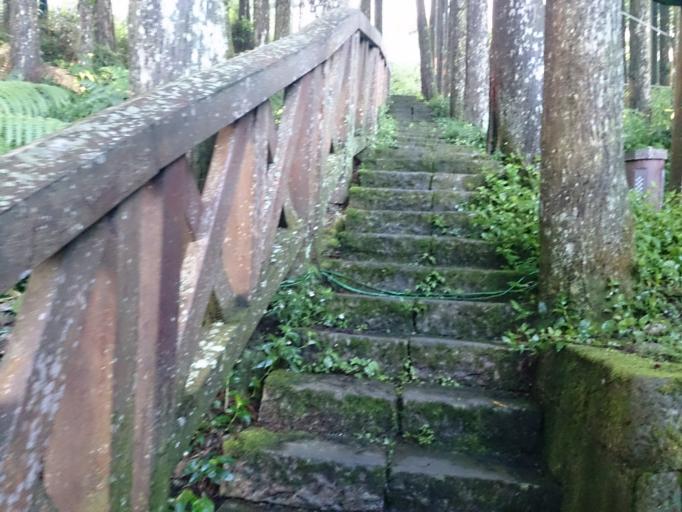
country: TW
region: Taiwan
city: Lugu
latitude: 23.5119
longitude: 120.8039
